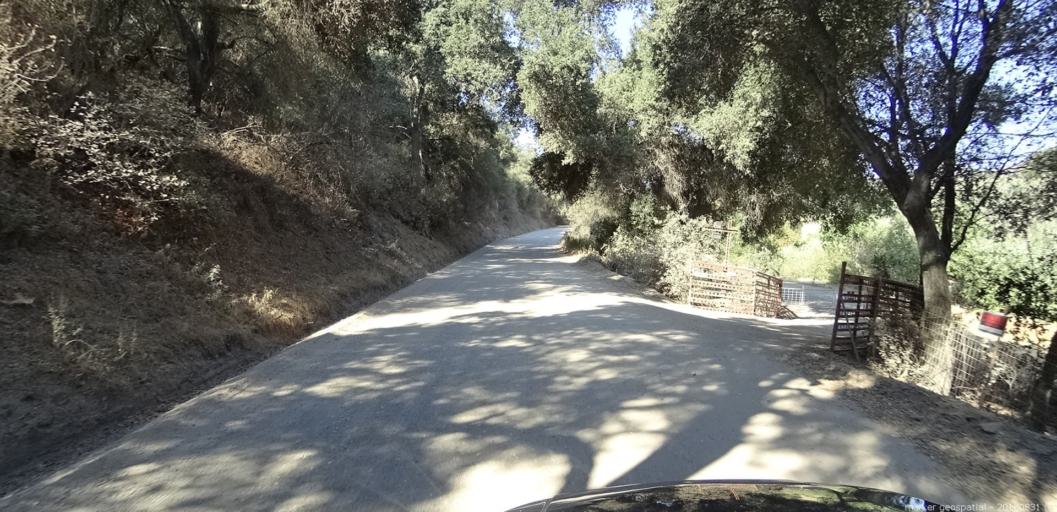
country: US
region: California
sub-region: Monterey County
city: King City
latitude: 36.1433
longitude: -121.2051
